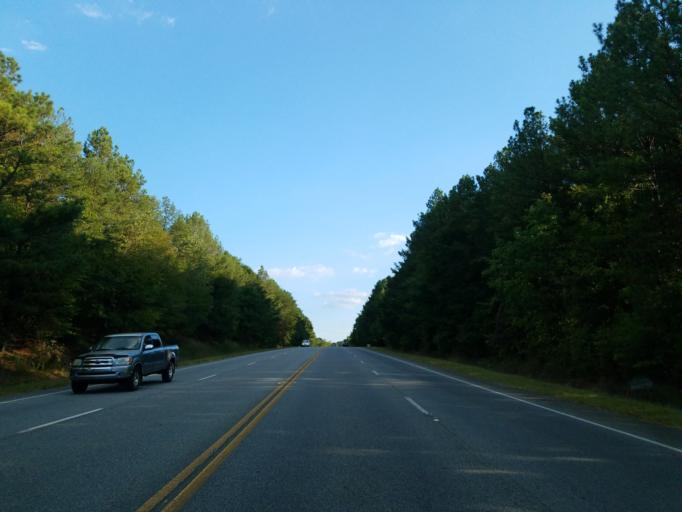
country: US
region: Georgia
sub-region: Murray County
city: Chatsworth
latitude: 34.7191
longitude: -84.7465
